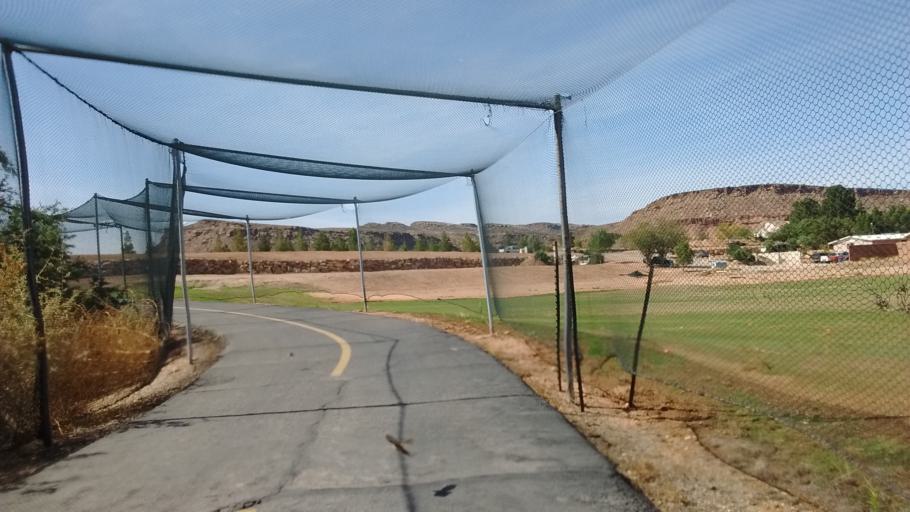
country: US
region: Utah
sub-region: Washington County
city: Saint George
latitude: 37.0556
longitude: -113.6013
